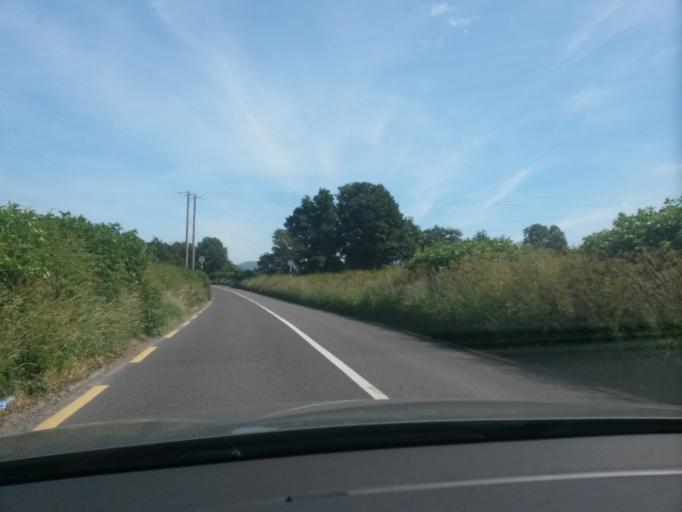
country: IE
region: Leinster
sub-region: Wicklow
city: Blessington
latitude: 53.1742
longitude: -6.5550
